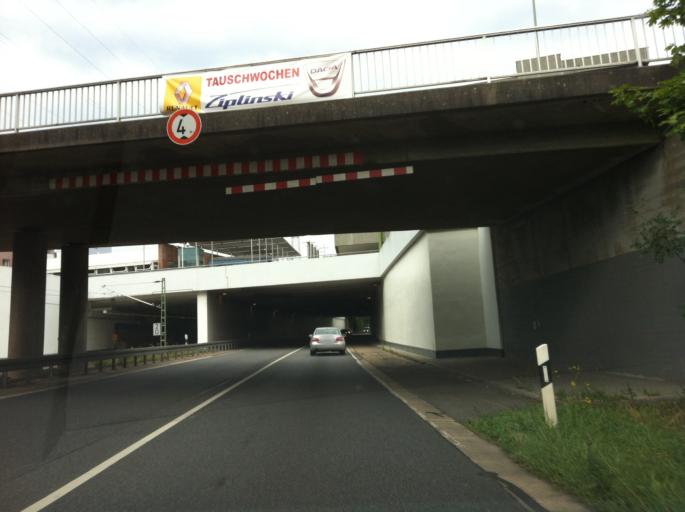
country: DE
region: Hesse
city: Schwalbach am Taunus
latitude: 50.1523
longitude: 8.5269
